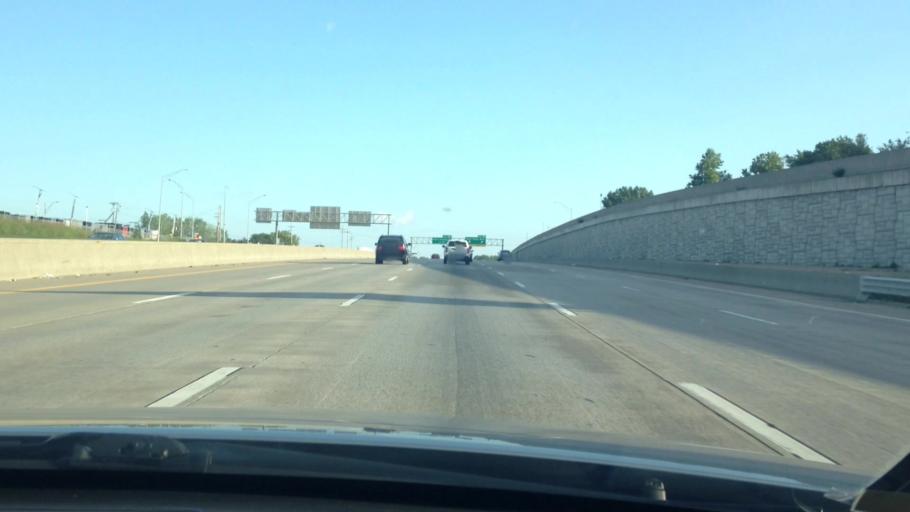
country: US
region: Missouri
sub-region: Jackson County
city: Grandview
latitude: 38.9141
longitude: -94.5260
